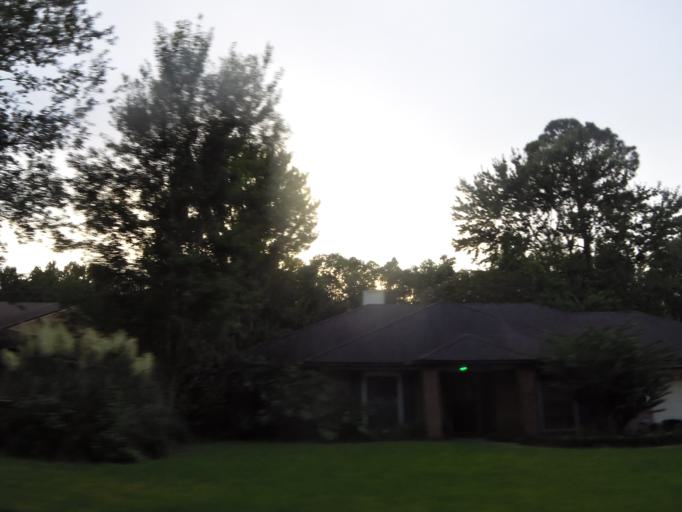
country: US
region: Florida
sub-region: Duval County
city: Atlantic Beach
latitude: 30.3552
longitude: -81.4970
